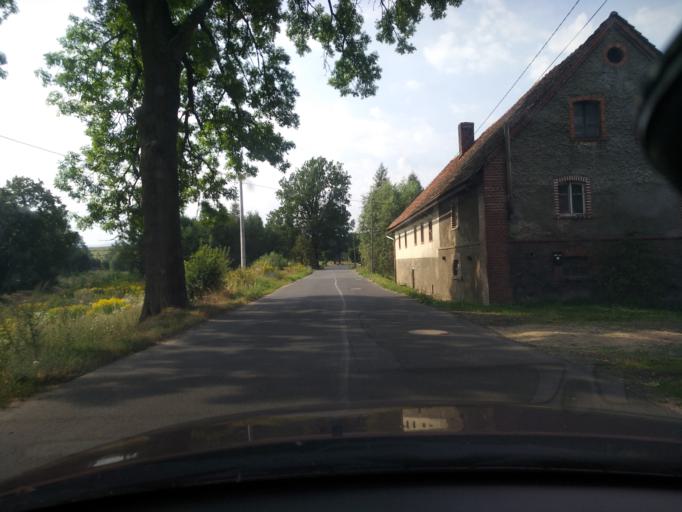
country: PL
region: Lower Silesian Voivodeship
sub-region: Powiat jeleniogorski
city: Stara Kamienica
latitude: 50.9338
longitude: 15.5828
